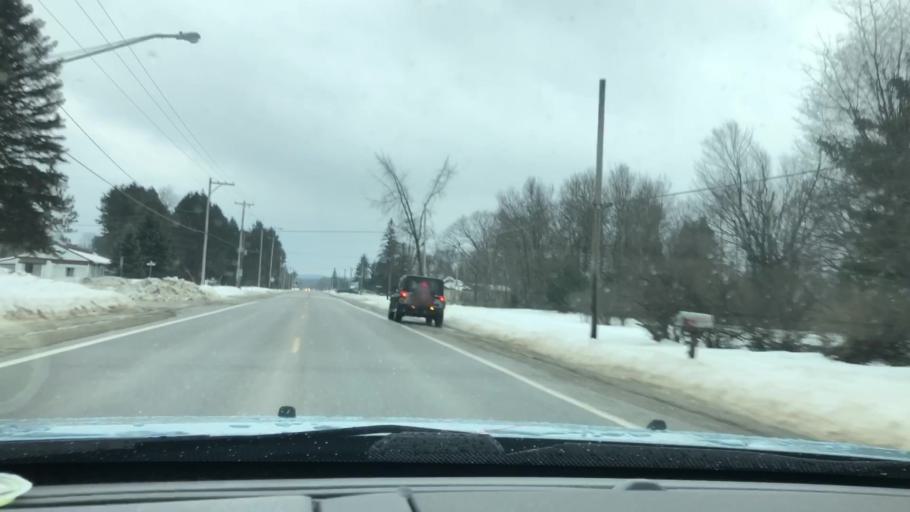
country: US
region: Michigan
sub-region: Charlevoix County
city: East Jordan
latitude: 45.1444
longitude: -85.1192
